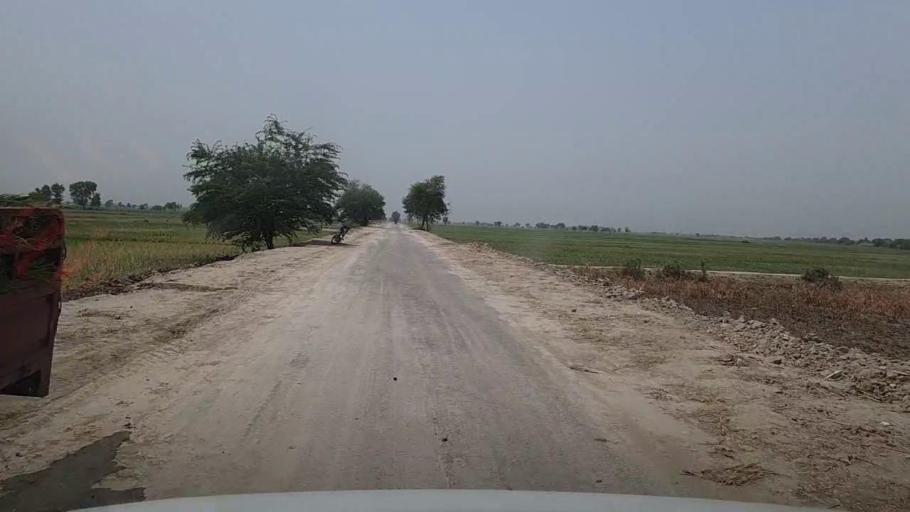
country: PK
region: Sindh
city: Sita Road
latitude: 27.0893
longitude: 67.9136
